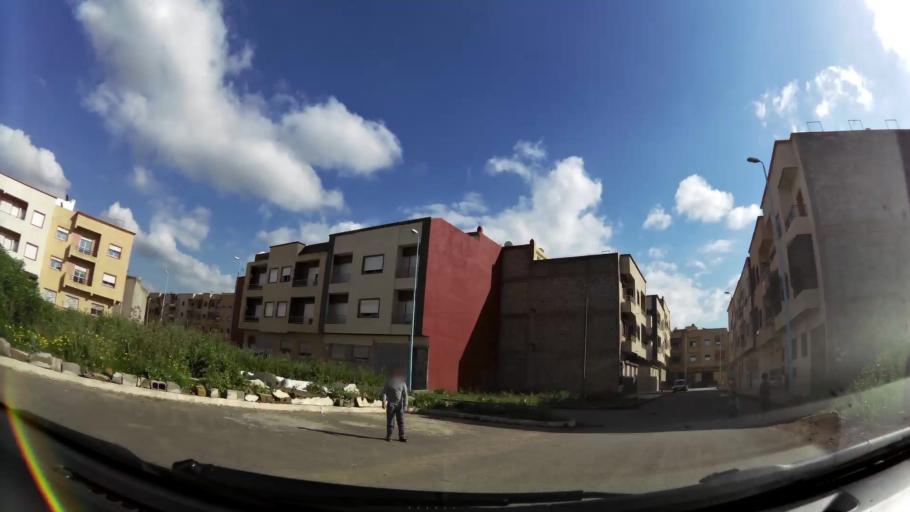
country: MA
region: Grand Casablanca
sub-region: Mediouna
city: Mediouna
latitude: 33.3872
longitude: -7.5303
